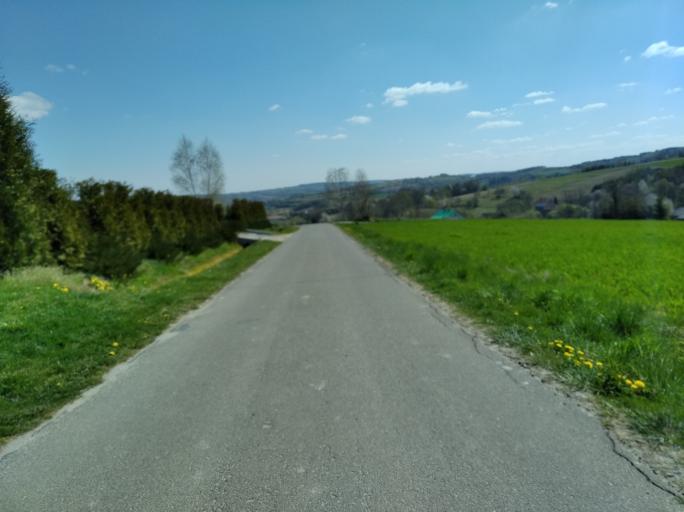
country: PL
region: Subcarpathian Voivodeship
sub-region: Powiat strzyzowski
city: Wisniowa
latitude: 49.9095
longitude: 21.6650
